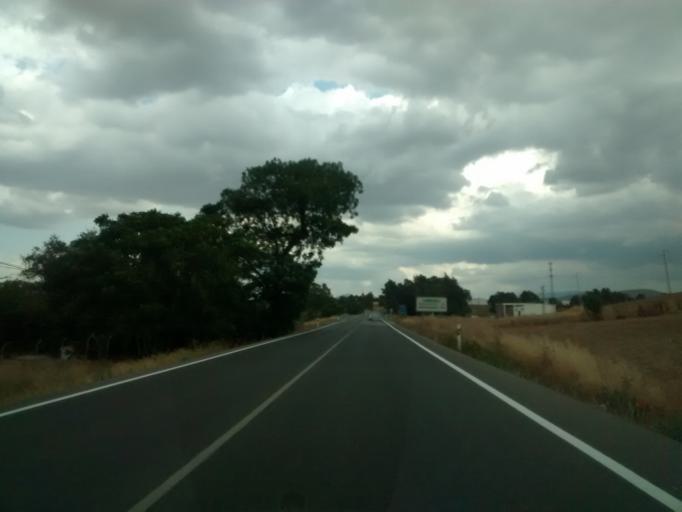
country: ES
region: Andalusia
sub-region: Provincia de Cadiz
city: Villamartin
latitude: 36.8581
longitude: -5.6257
